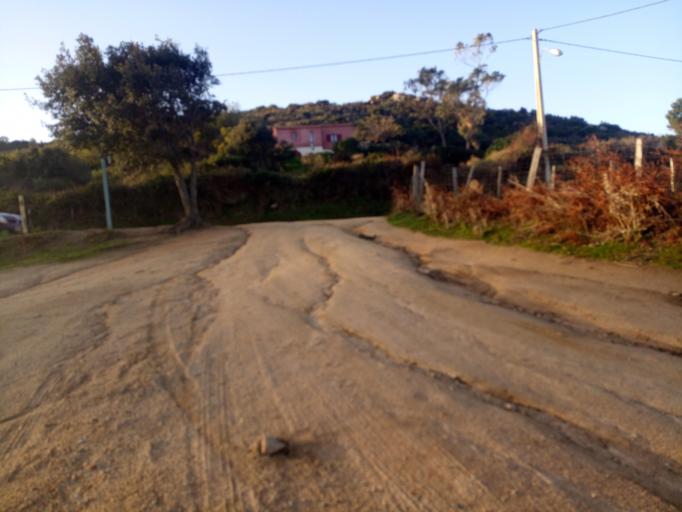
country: FR
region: Corsica
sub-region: Departement de la Corse-du-Sud
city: Appietto
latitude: 42.0705
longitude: 8.7273
